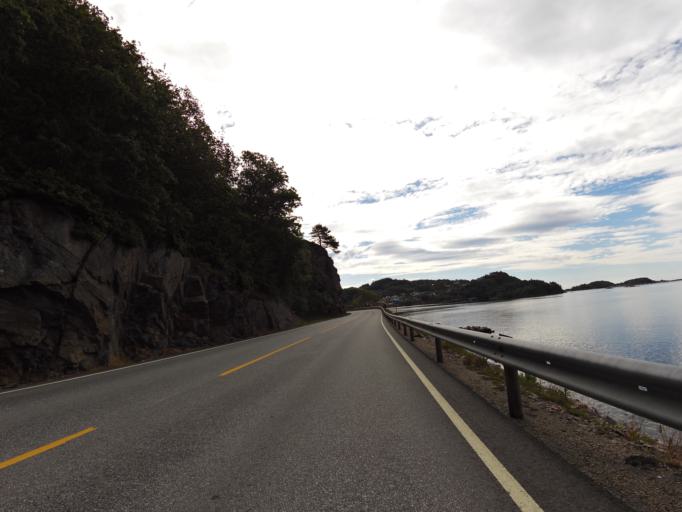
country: NO
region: Vest-Agder
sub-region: Lindesnes
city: Vigeland
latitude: 58.0510
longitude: 7.1859
